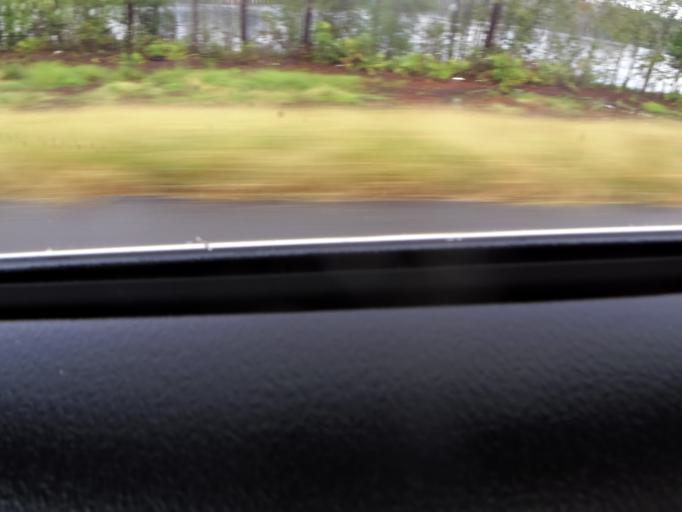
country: US
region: Georgia
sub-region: Wayne County
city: Jesup
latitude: 31.6247
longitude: -81.8671
